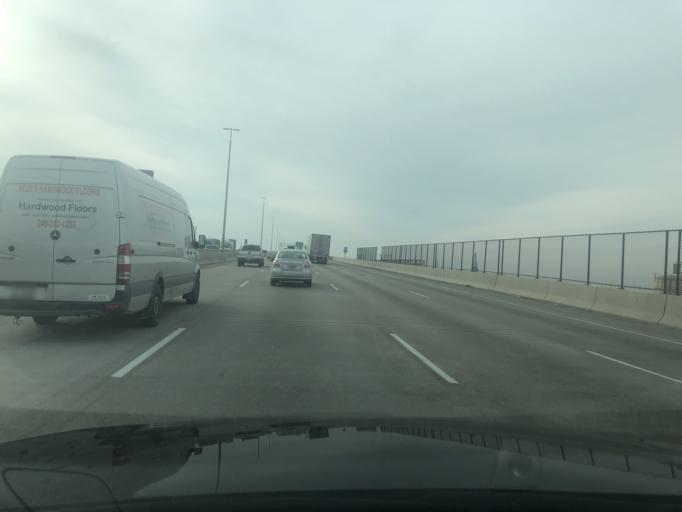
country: US
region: Michigan
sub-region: Wayne County
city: River Rouge
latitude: 42.2893
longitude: -83.1346
